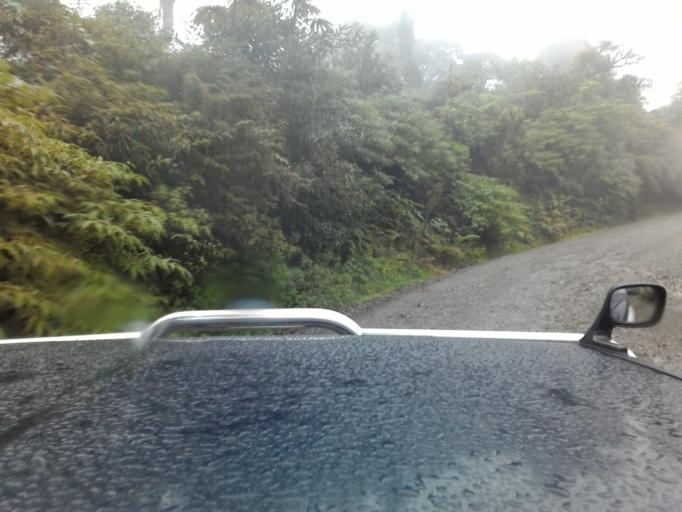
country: CR
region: Guanacaste
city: Juntas
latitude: 10.3439
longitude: -84.8019
